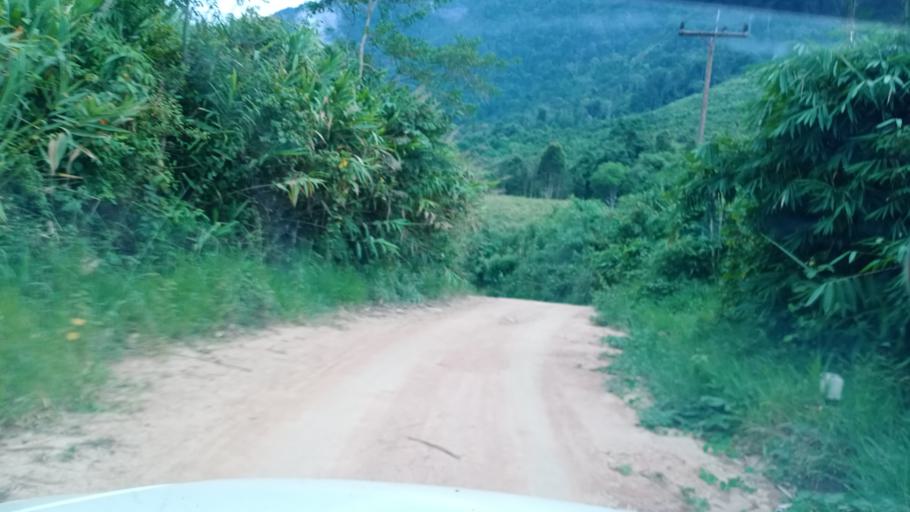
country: TH
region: Changwat Bueng Kan
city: Pak Khat
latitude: 18.7241
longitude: 103.2776
